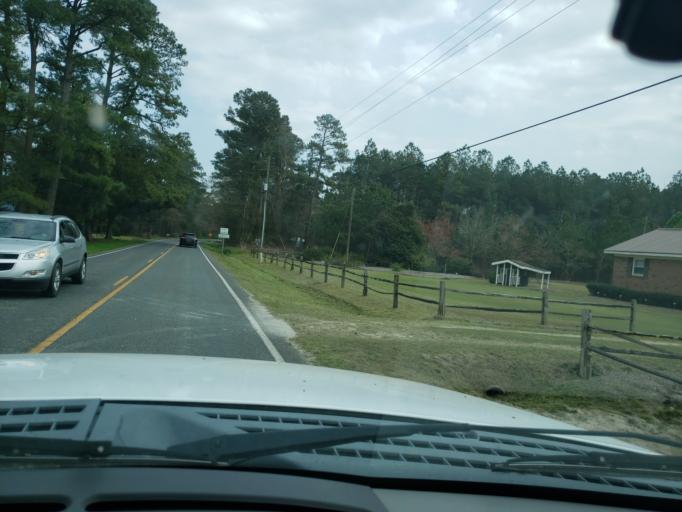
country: US
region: North Carolina
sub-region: Duplin County
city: Beulaville
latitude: 34.7581
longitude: -77.7915
